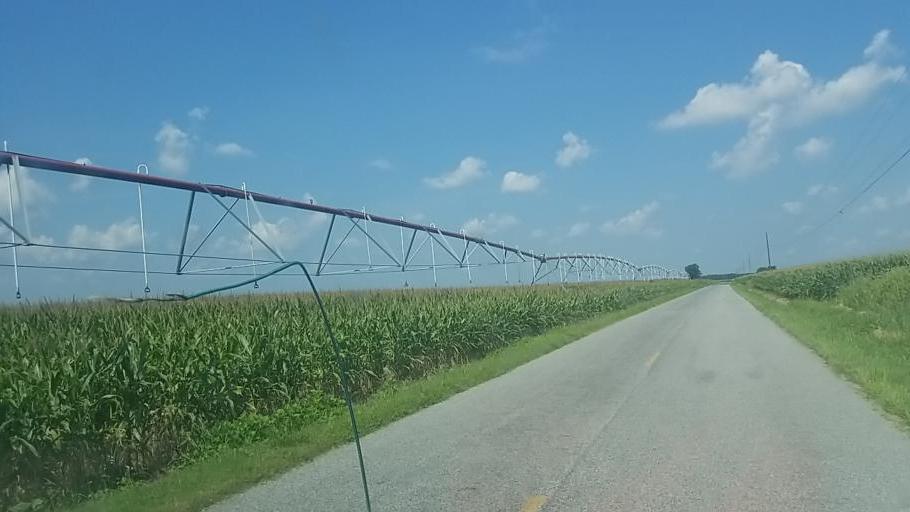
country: US
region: Maryland
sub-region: Worcester County
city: Berlin
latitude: 38.2898
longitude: -75.2424
